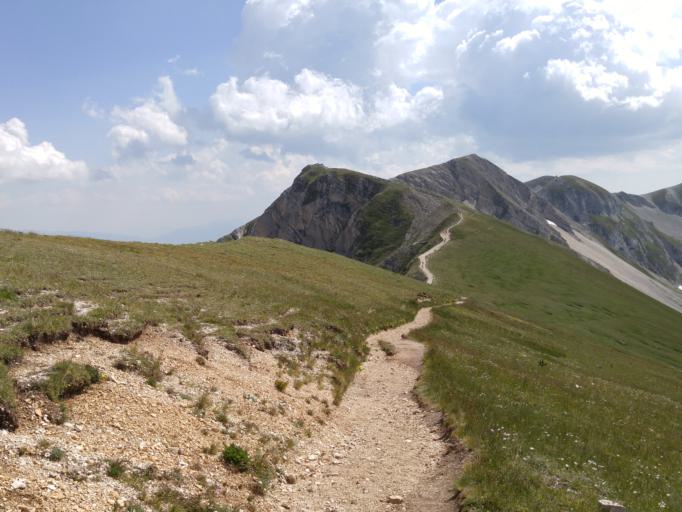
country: IT
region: Abruzzo
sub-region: Provincia di Teramo
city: Pietracamela
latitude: 42.4573
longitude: 13.5609
